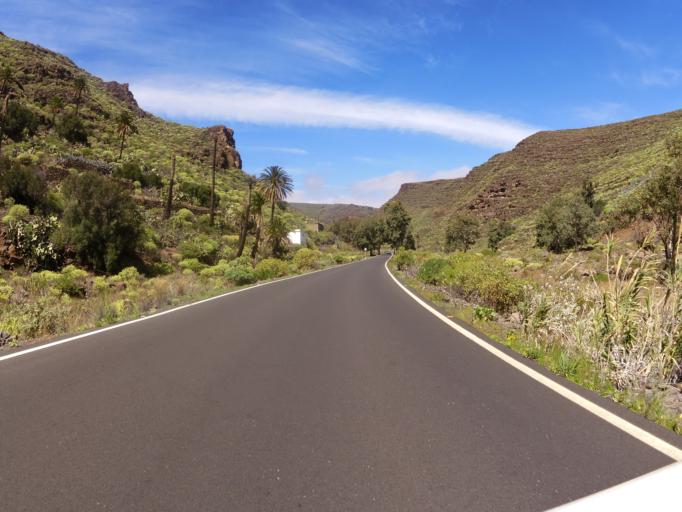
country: ES
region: Canary Islands
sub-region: Provincia de Las Palmas
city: Ingenio
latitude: 27.9206
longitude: -15.4585
